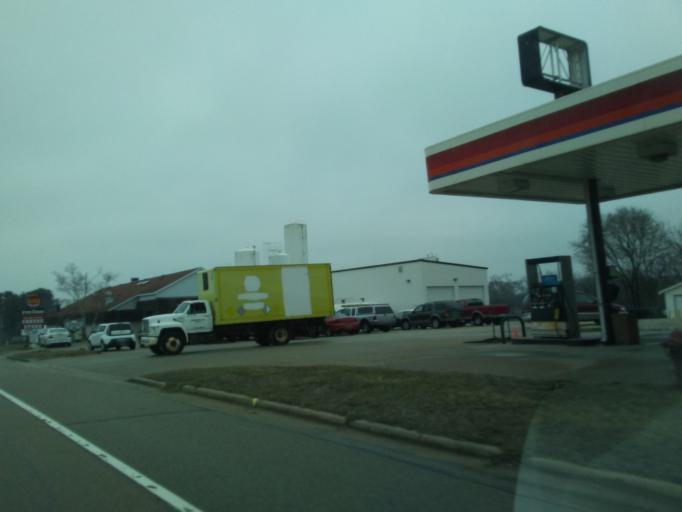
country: US
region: Wisconsin
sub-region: Dane County
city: Mazomanie
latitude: 43.1616
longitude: -89.9066
